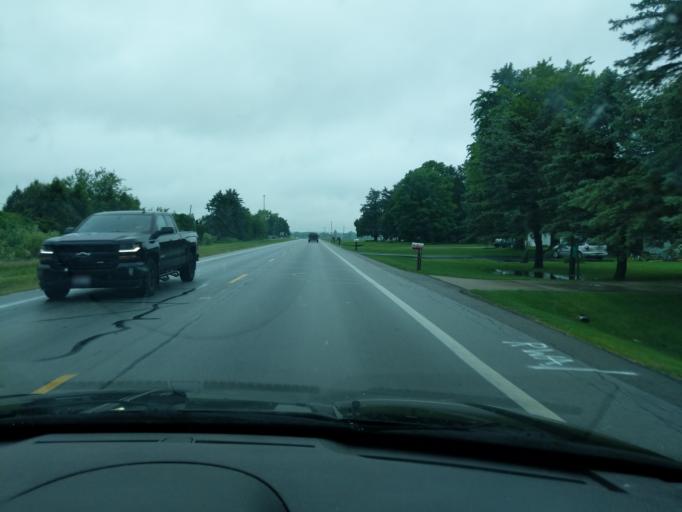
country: US
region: Ohio
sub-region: Logan County
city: West Liberty
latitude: 40.2329
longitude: -83.7519
